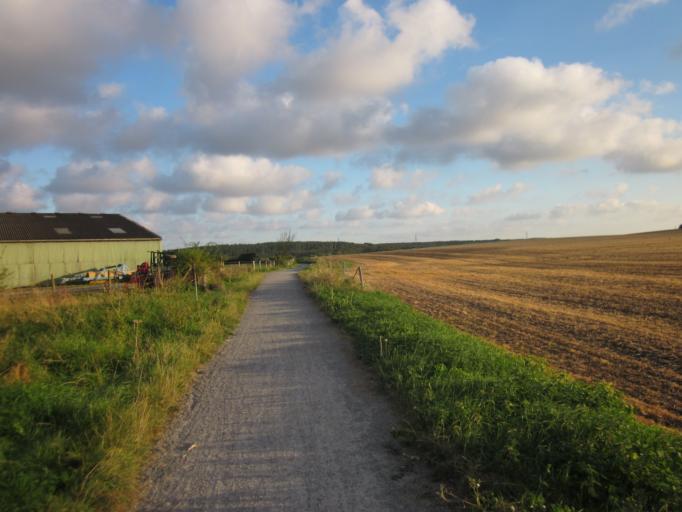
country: GB
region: England
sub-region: Kent
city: Tankerton
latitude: 51.3445
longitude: 1.0477
